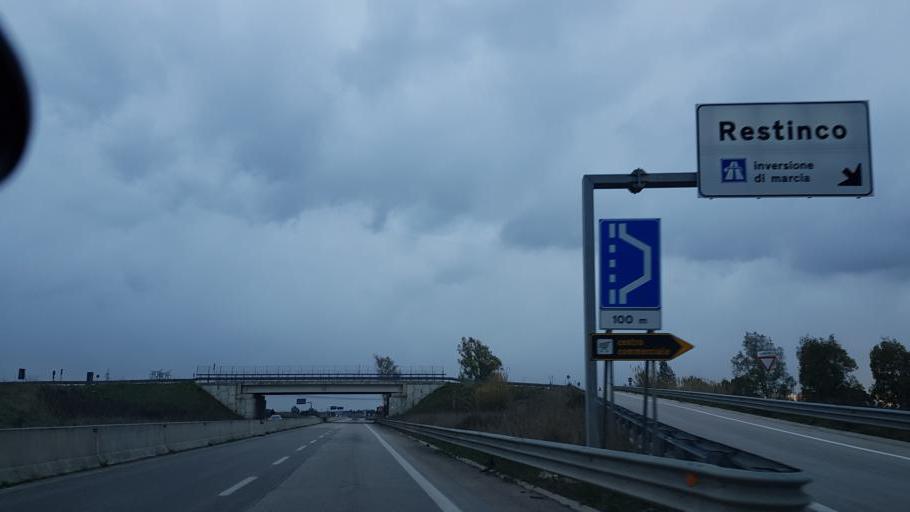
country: IT
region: Apulia
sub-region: Provincia di Brindisi
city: Brindisi
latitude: 40.6052
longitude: 17.8841
